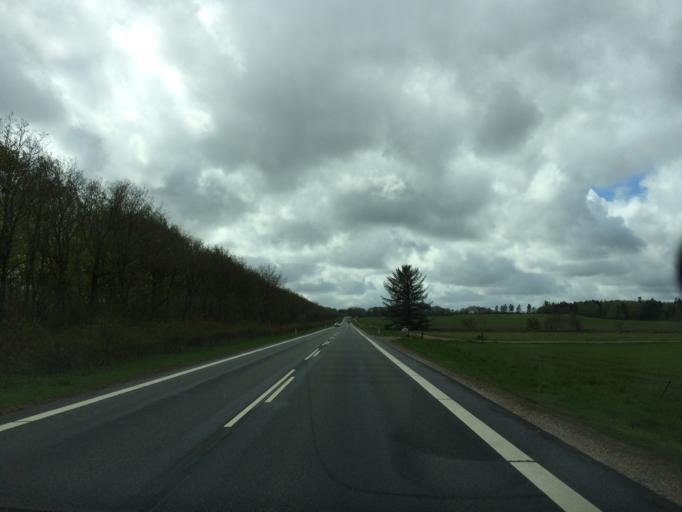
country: DK
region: Central Jutland
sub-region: Viborg Kommune
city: Viborg
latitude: 56.4452
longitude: 9.2803
